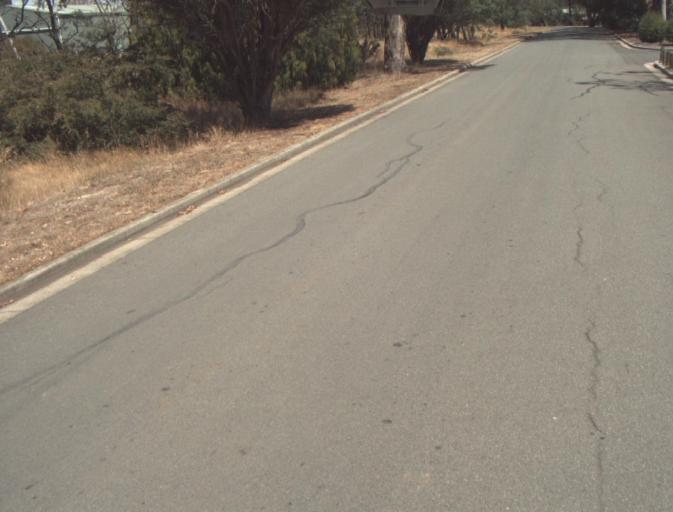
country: AU
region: Tasmania
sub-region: Launceston
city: Mayfield
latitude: -41.3738
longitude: 147.1323
